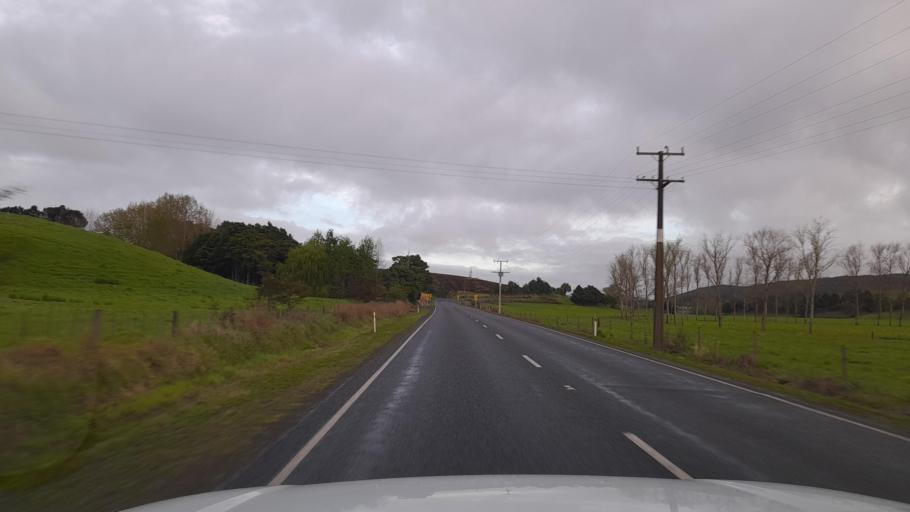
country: NZ
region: Northland
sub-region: Whangarei
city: Maungatapere
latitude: -35.7111
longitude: 174.0284
